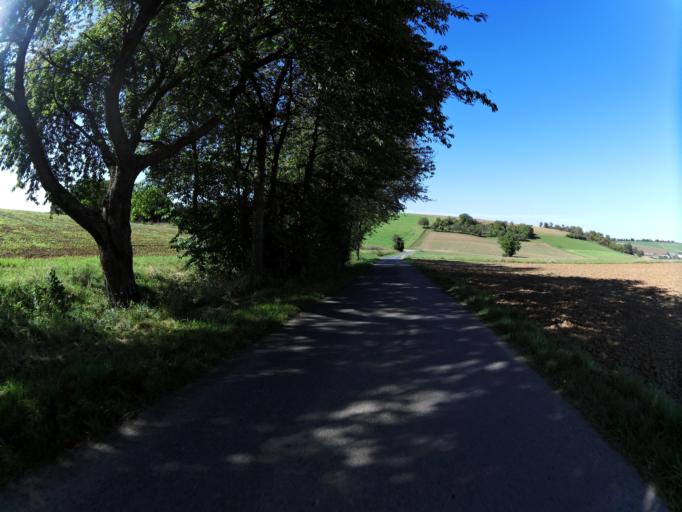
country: DE
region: Bavaria
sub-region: Regierungsbezirk Unterfranken
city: Waldbrunn
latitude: 49.7197
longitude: 9.7723
